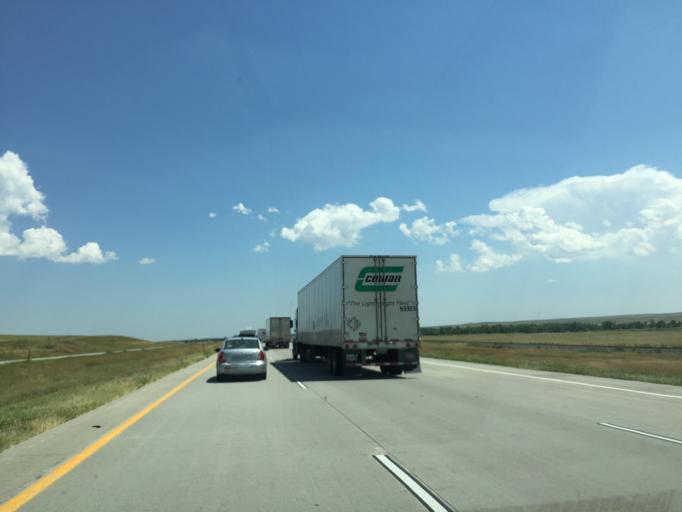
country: US
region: Colorado
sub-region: Lincoln County
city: Limon
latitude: 39.2895
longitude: -103.7924
